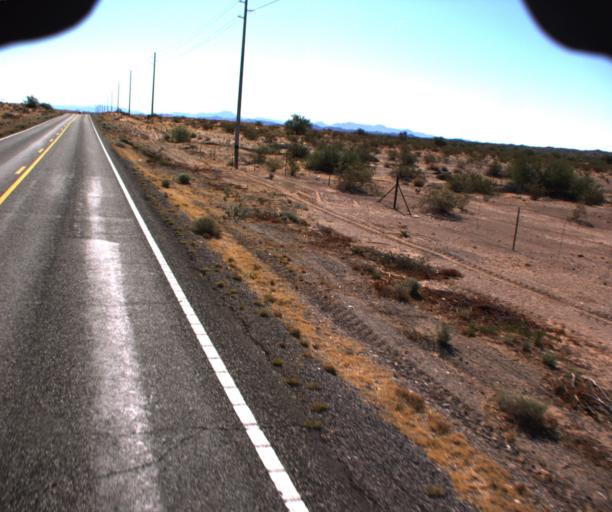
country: US
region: Arizona
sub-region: La Paz County
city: Cienega Springs
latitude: 33.9936
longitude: -114.1118
